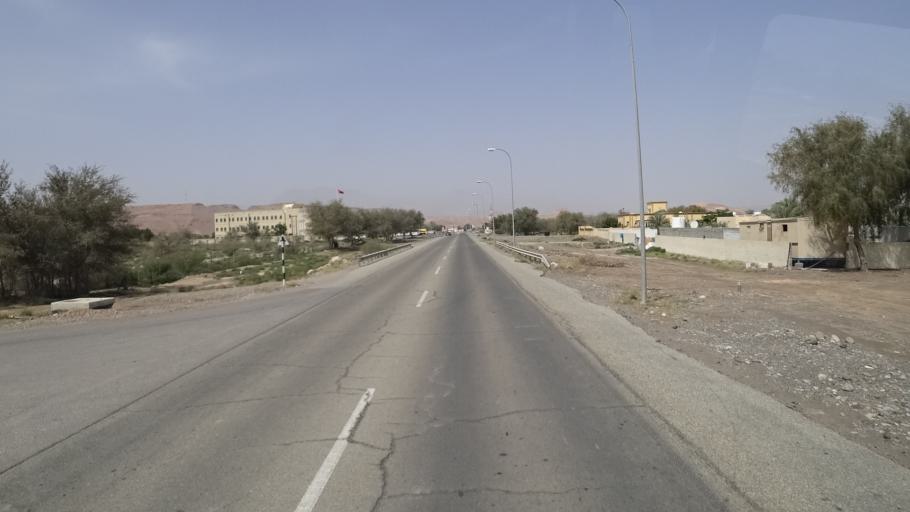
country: OM
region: Muhafazat Masqat
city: Muscat
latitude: 23.2062
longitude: 58.9599
